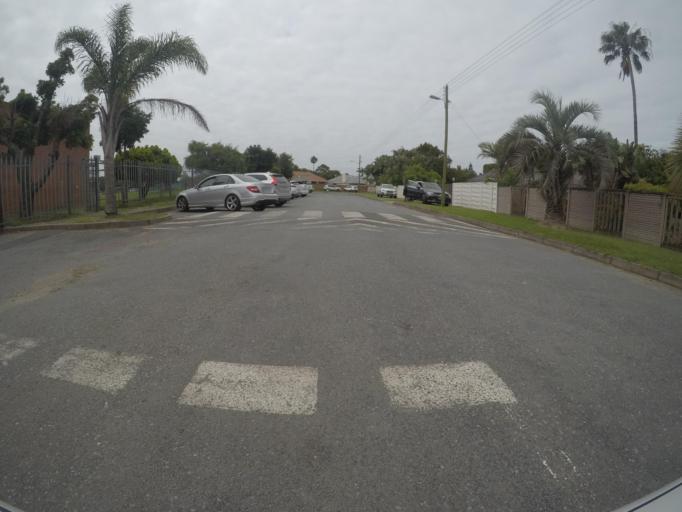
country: ZA
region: Eastern Cape
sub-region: Buffalo City Metropolitan Municipality
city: East London
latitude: -32.9705
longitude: 27.9367
